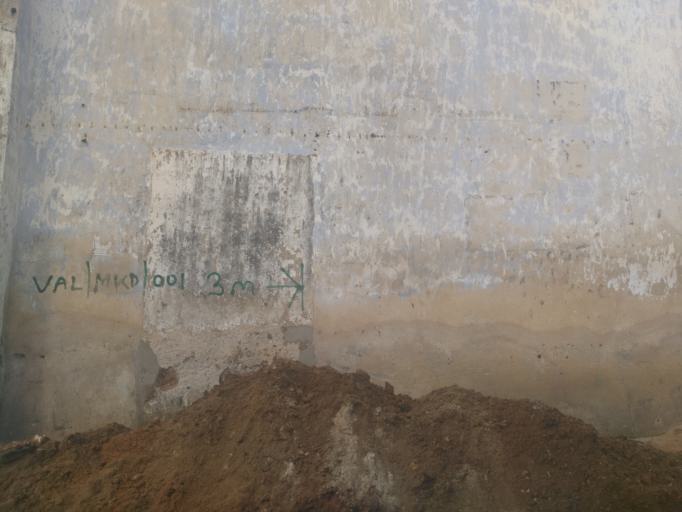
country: TZ
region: Zanzibar Urban/West
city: Zanzibar
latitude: -6.1589
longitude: 39.2093
